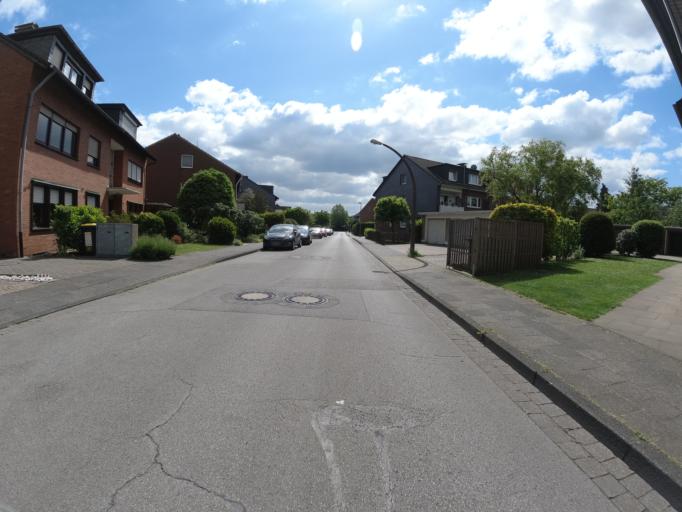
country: DE
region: North Rhine-Westphalia
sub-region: Regierungsbezirk Dusseldorf
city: Hochfeld
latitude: 51.3950
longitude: 6.7032
